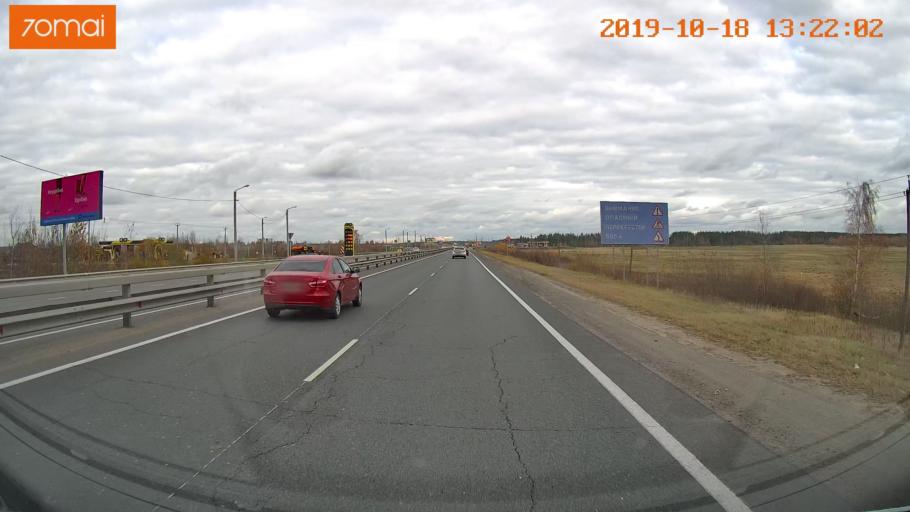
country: RU
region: Rjazan
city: Polyany
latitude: 54.7032
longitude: 39.8435
